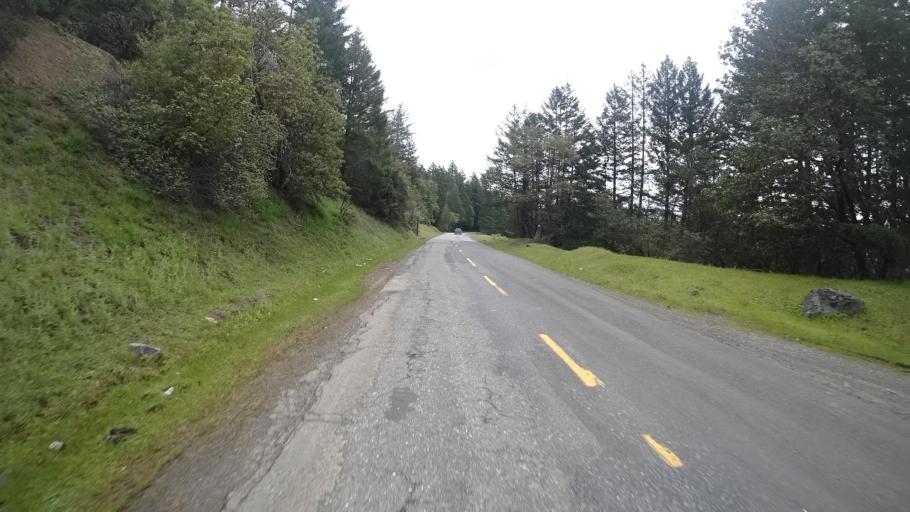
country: US
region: California
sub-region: Humboldt County
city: Redway
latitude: 40.1221
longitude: -123.6643
